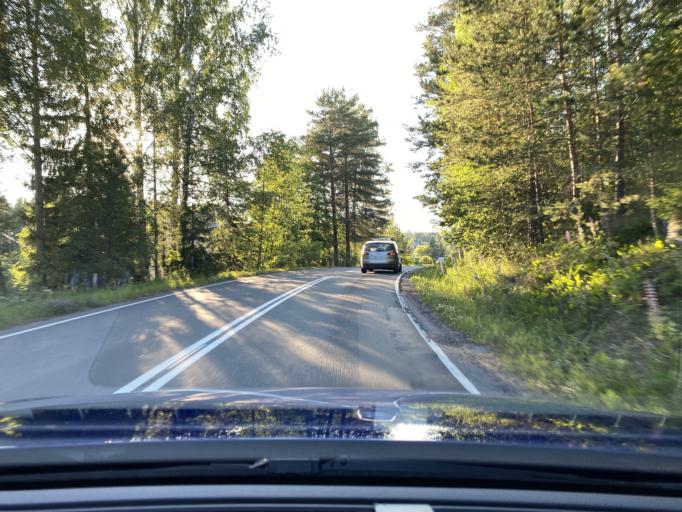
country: FI
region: Haeme
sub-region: Riihimaeki
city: Riihimaeki
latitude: 60.7192
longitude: 24.7074
